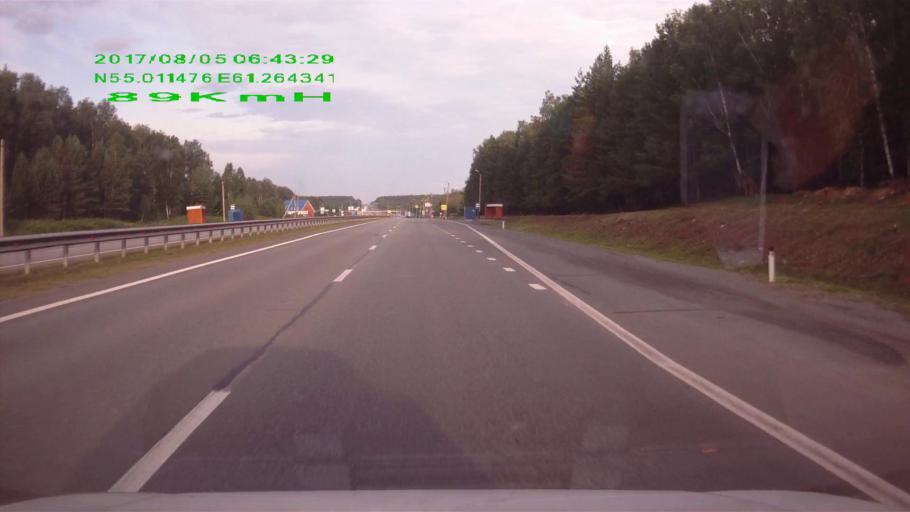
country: RU
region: Chelyabinsk
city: Sargazy
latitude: 55.0115
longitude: 61.2637
